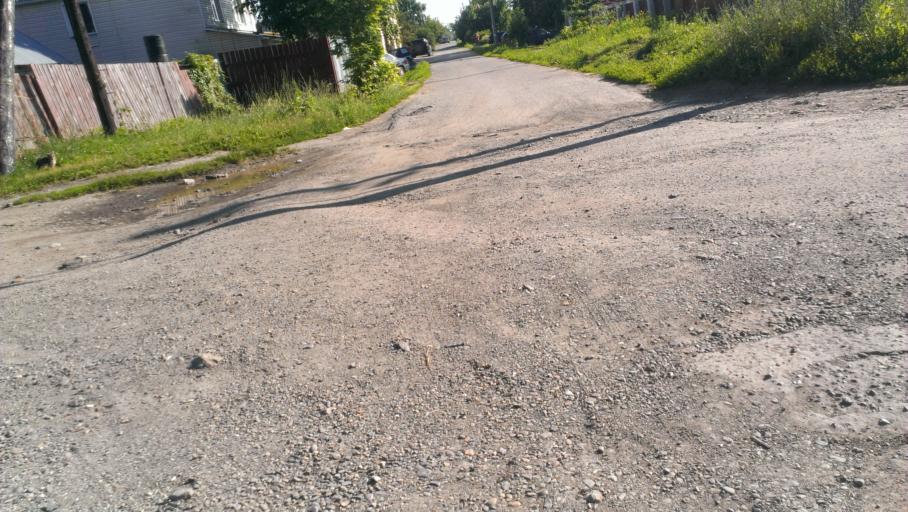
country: RU
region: Altai Krai
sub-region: Gorod Barnaulskiy
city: Barnaul
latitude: 53.3566
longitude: 83.7406
